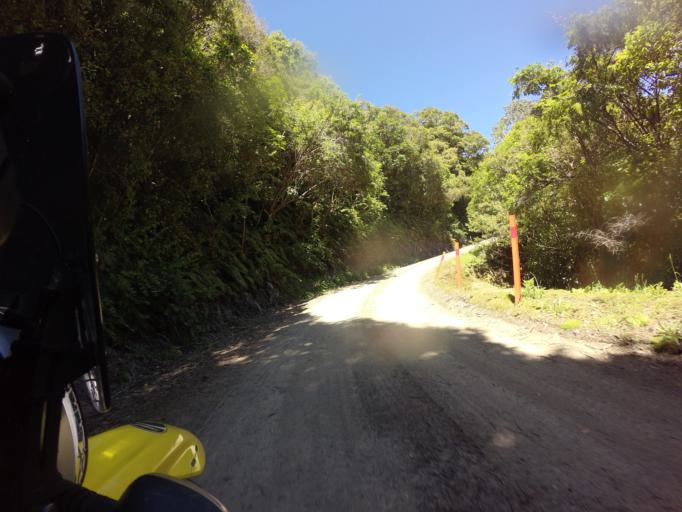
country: NZ
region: Bay of Plenty
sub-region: Opotiki District
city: Opotiki
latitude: -38.4096
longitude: 177.4166
